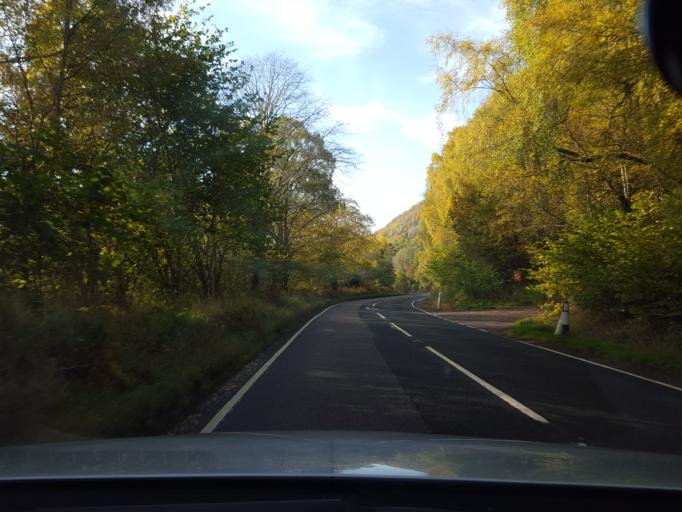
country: GB
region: Scotland
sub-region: Highland
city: Beauly
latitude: 57.3135
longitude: -4.4557
